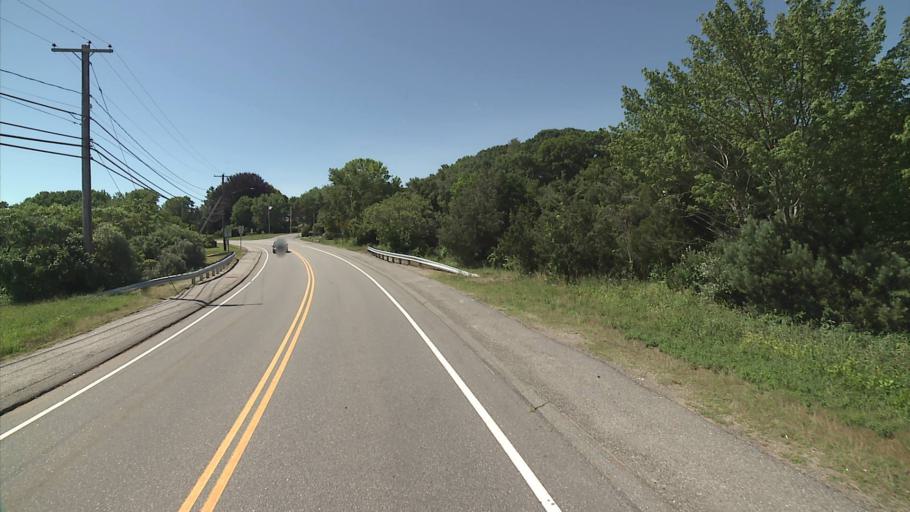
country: US
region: Connecticut
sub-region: New London County
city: Noank
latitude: 41.3328
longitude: -71.9927
